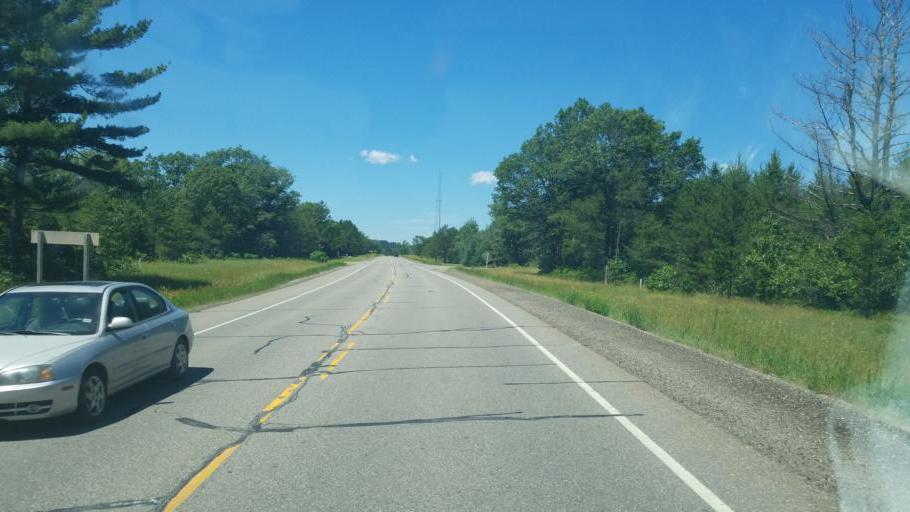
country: US
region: Wisconsin
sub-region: Adams County
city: Friendship
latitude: 44.0469
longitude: -89.9742
